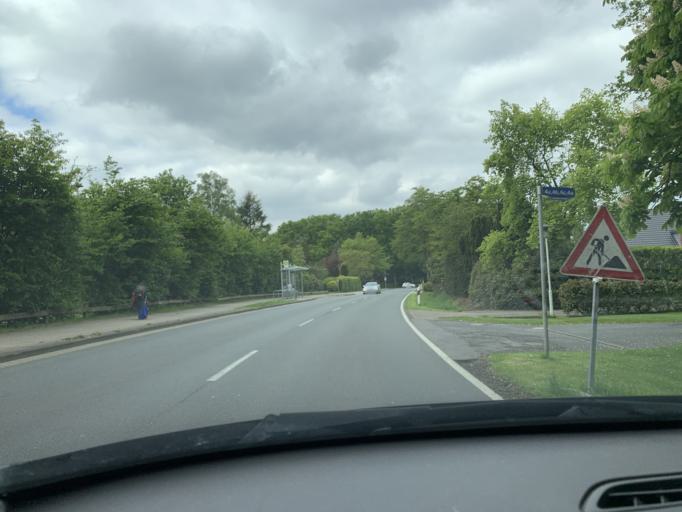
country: DE
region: Lower Saxony
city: Bad Zwischenahn
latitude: 53.1948
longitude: 8.0470
